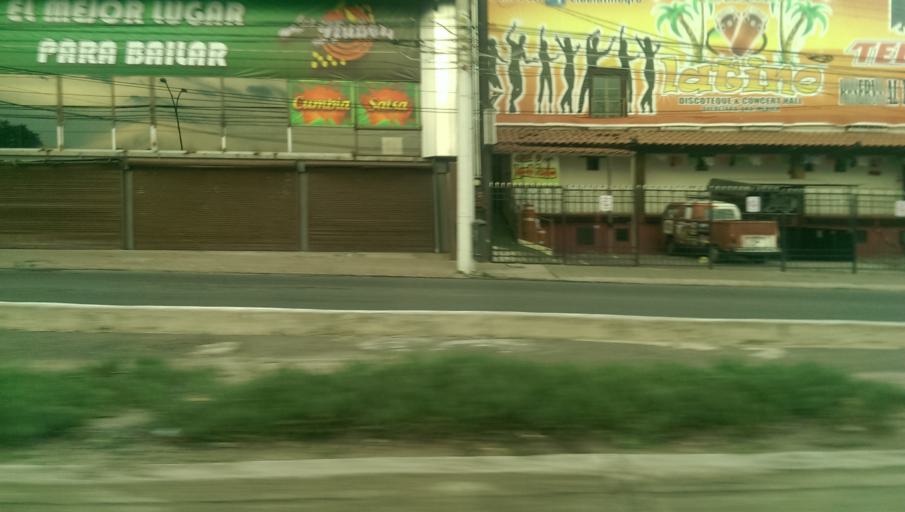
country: MX
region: Queretaro
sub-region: Queretaro
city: Santiago de Queretaro
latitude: 20.5919
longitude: -100.3674
